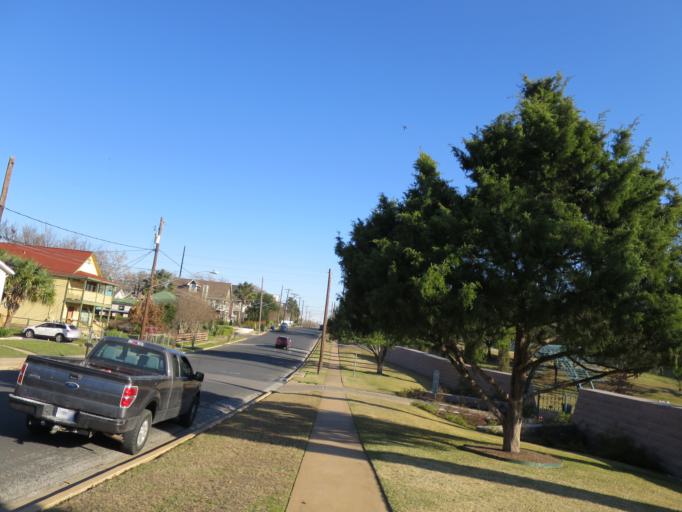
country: US
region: Texas
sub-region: Travis County
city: Austin
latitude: 30.2679
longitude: -97.7259
